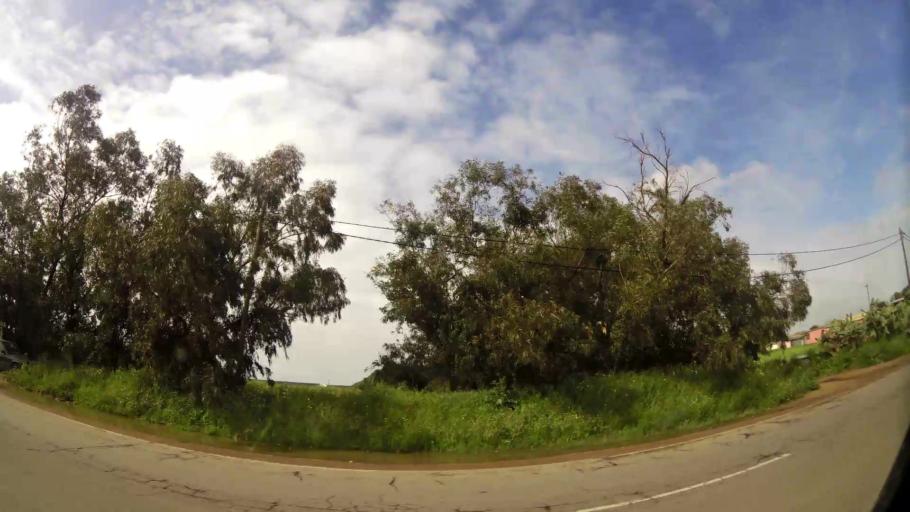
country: MA
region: Grand Casablanca
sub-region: Mohammedia
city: Mohammedia
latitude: 33.6512
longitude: -7.4092
